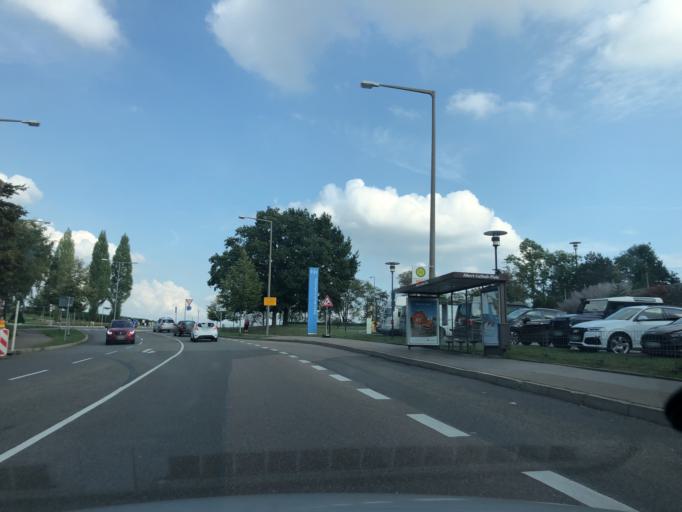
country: DE
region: Baden-Wuerttemberg
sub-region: Regierungsbezirk Stuttgart
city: Stuttgart Feuerbach
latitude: 48.8158
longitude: 9.1866
